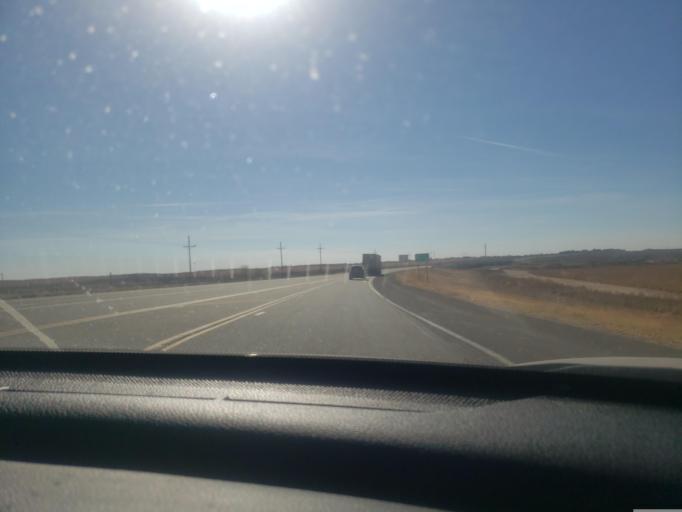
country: US
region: Kansas
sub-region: Finney County
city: Garden City
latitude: 37.9544
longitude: -100.8405
